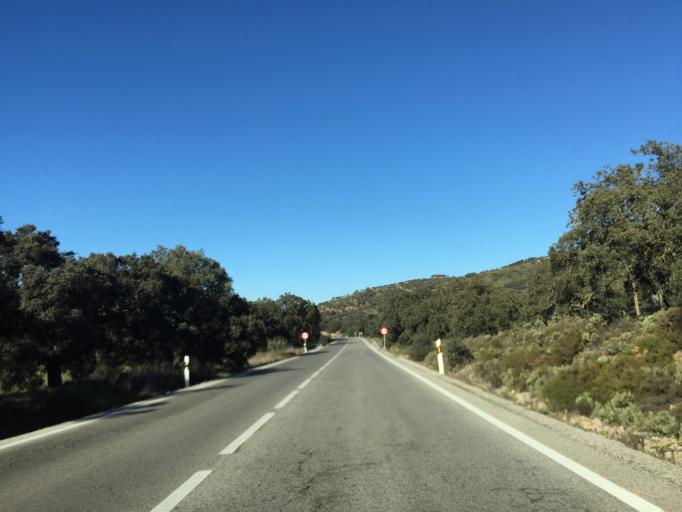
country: ES
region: Andalusia
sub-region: Provincia de Malaga
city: Cuevas del Becerro
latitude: 36.8315
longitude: -5.0818
